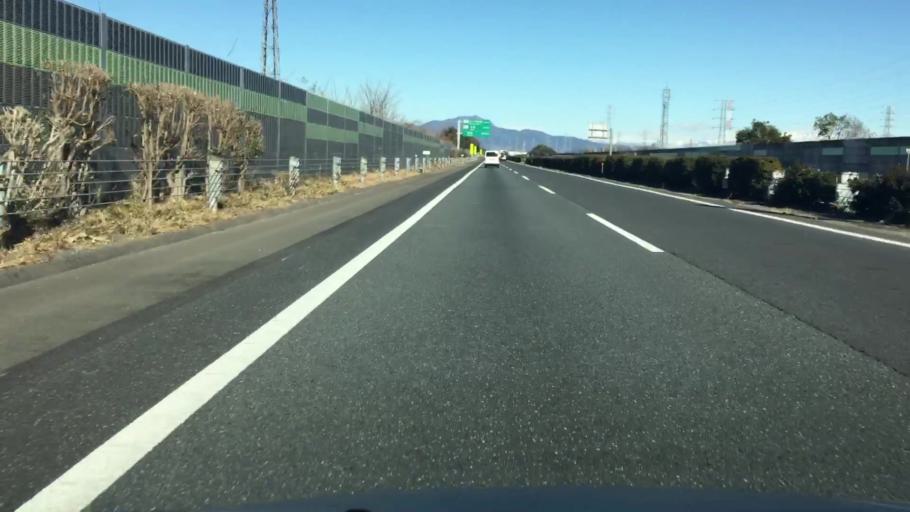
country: JP
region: Gunma
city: Maebashi-shi
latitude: 36.3845
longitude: 139.0264
